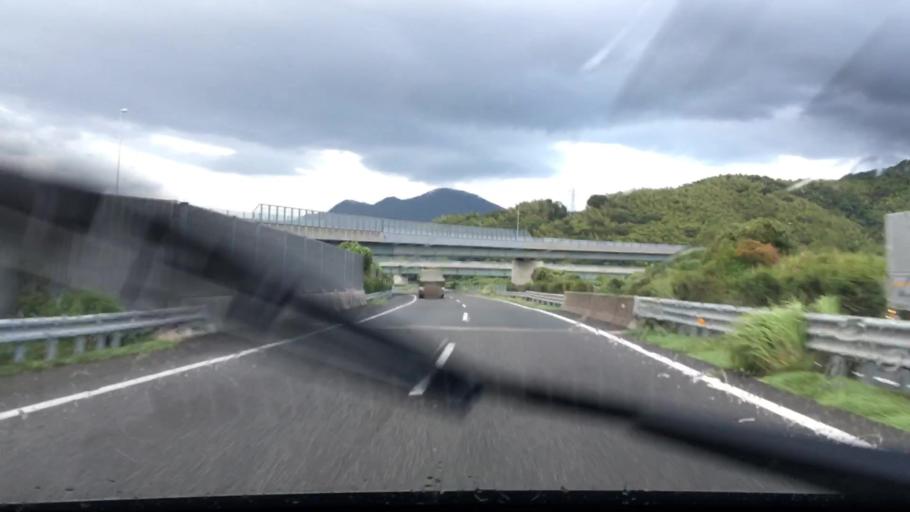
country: JP
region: Fukuoka
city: Kitakyushu
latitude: 33.8142
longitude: 130.8836
